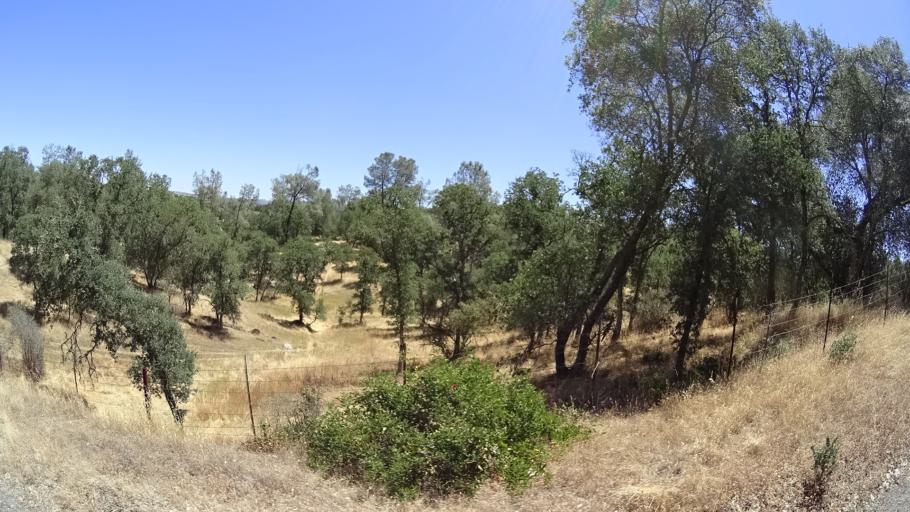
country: US
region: California
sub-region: Calaveras County
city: Copperopolis
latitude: 37.9839
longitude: -120.7017
